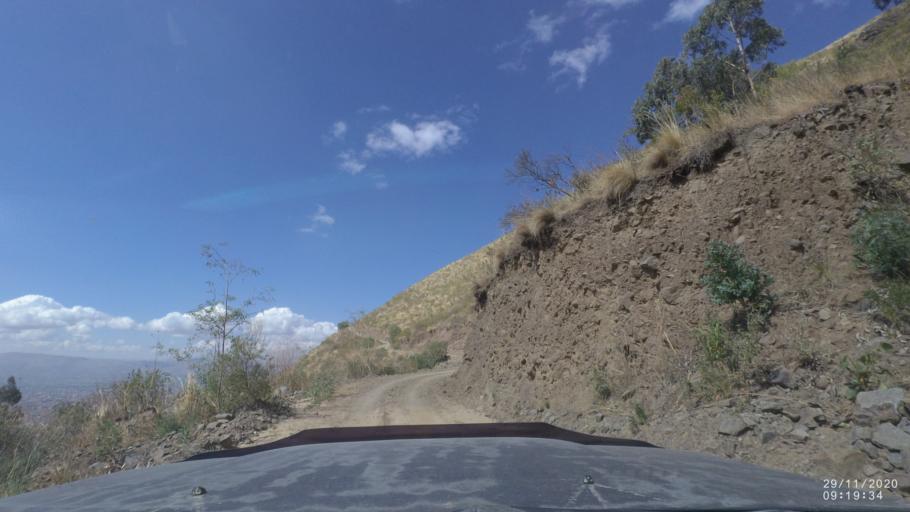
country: BO
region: Cochabamba
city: Cochabamba
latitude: -17.3223
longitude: -66.1836
